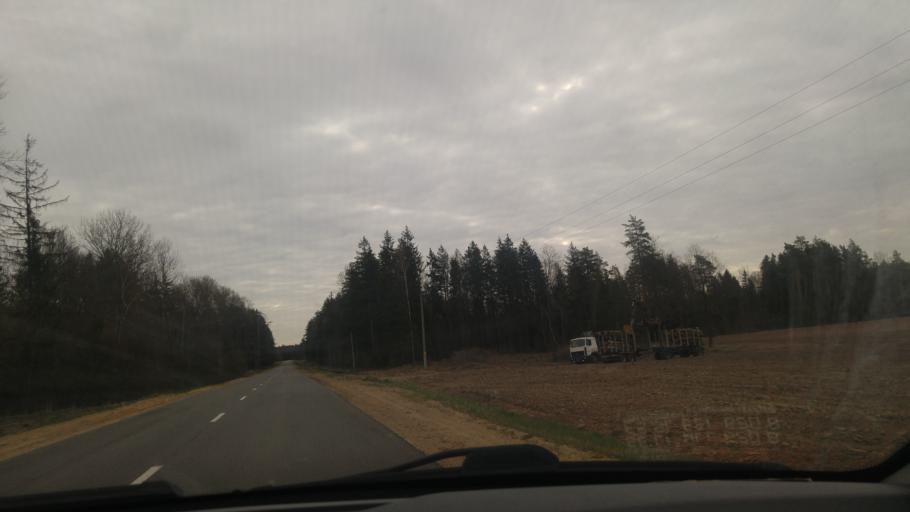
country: BY
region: Minsk
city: Chervyen'
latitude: 53.7331
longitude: 28.2886
